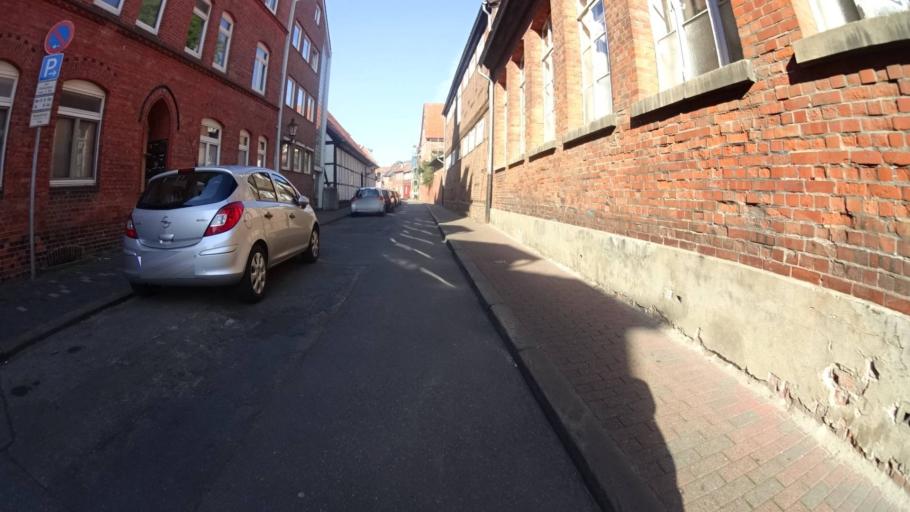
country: DE
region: Lower Saxony
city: Lueneburg
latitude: 53.2458
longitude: 10.4053
